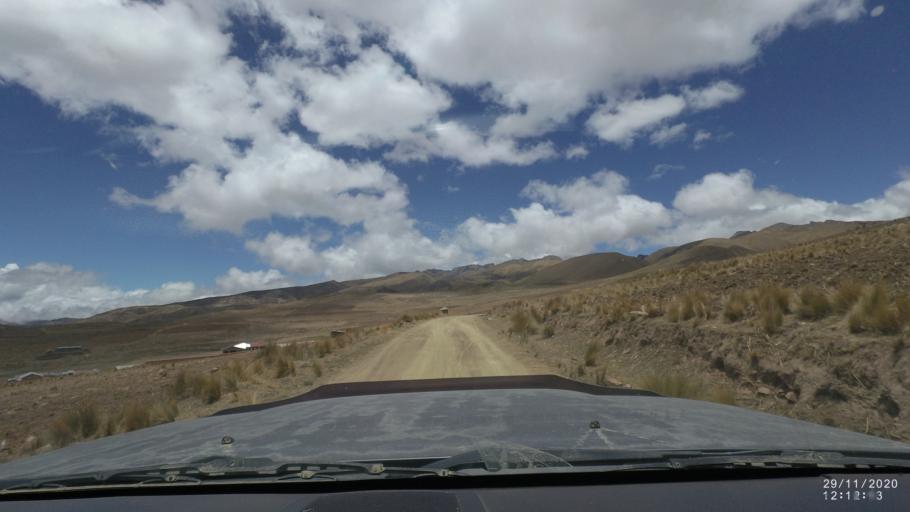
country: BO
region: Cochabamba
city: Cochabamba
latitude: -17.1139
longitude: -66.3034
